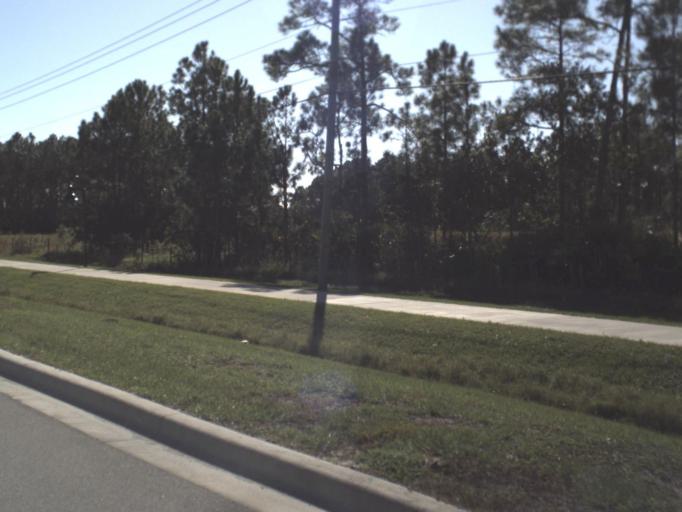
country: US
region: Florida
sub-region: Volusia County
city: Port Orange
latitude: 29.1096
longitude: -81.0373
